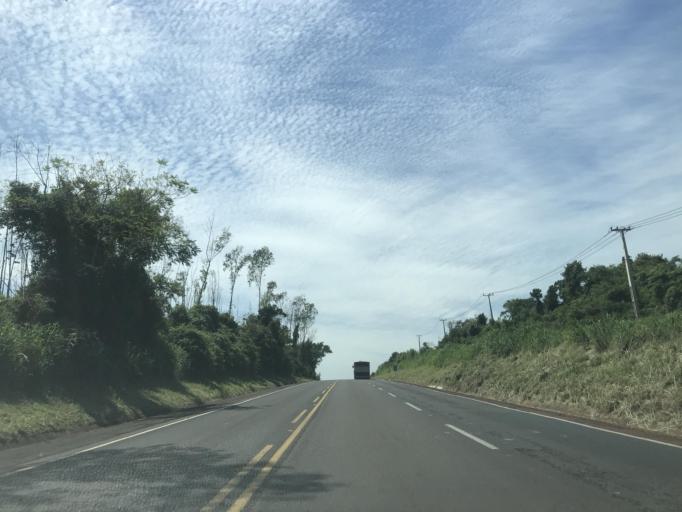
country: BR
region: Parana
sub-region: Paranavai
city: Nova Aurora
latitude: -22.9627
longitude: -52.6439
